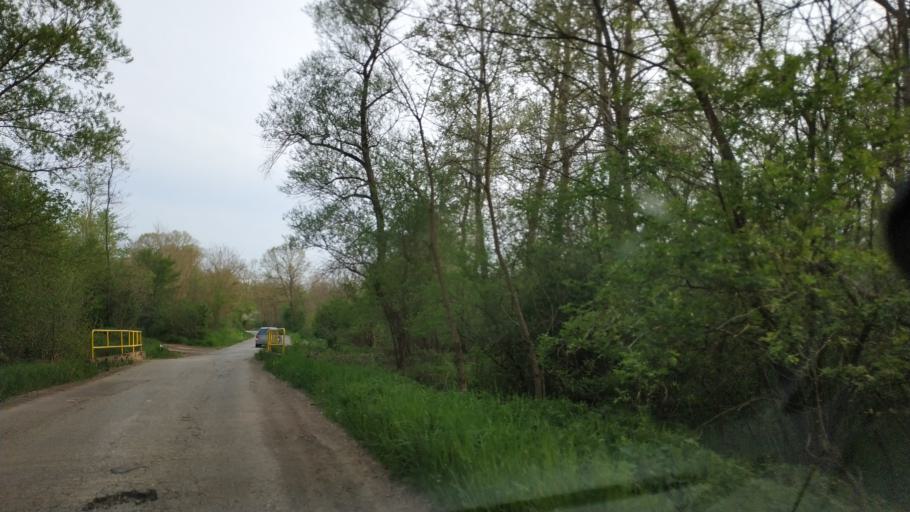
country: RS
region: Central Serbia
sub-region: Nisavski Okrug
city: Aleksinac
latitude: 43.4740
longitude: 21.8106
